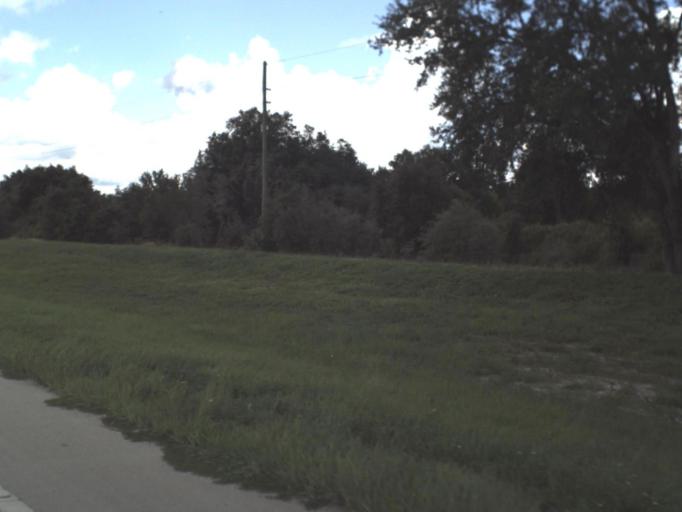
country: US
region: Florida
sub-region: DeSoto County
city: Southeast Arcadia
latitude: 27.2096
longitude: -81.6374
